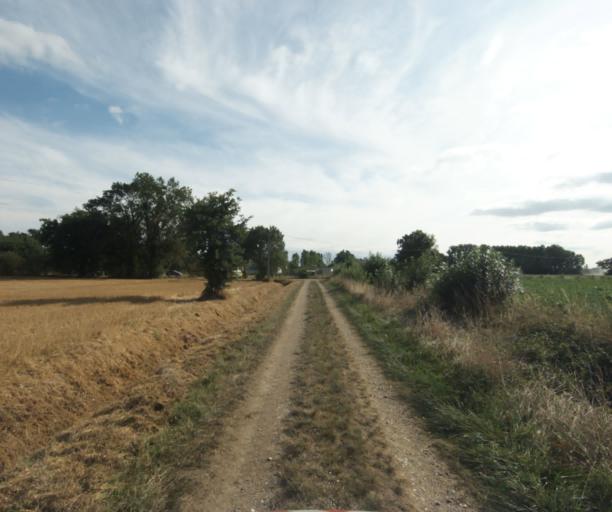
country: FR
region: Midi-Pyrenees
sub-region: Departement du Tarn
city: Puylaurens
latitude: 43.5198
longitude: 2.0009
